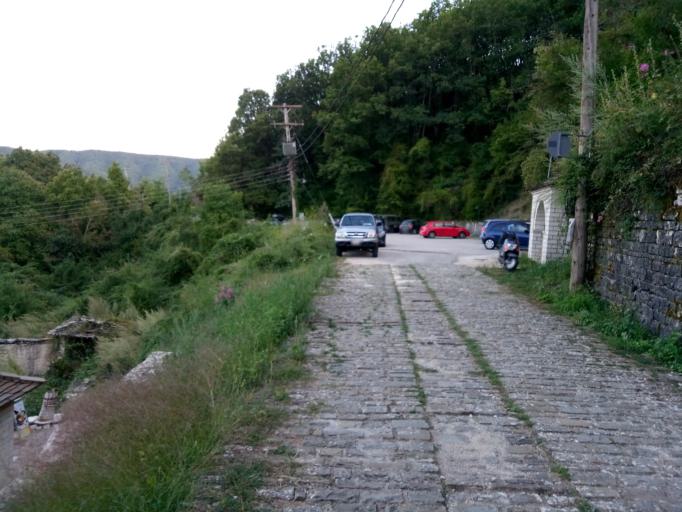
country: GR
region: Epirus
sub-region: Nomos Ioanninon
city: Asprangeloi
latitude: 39.8519
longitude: 20.7650
